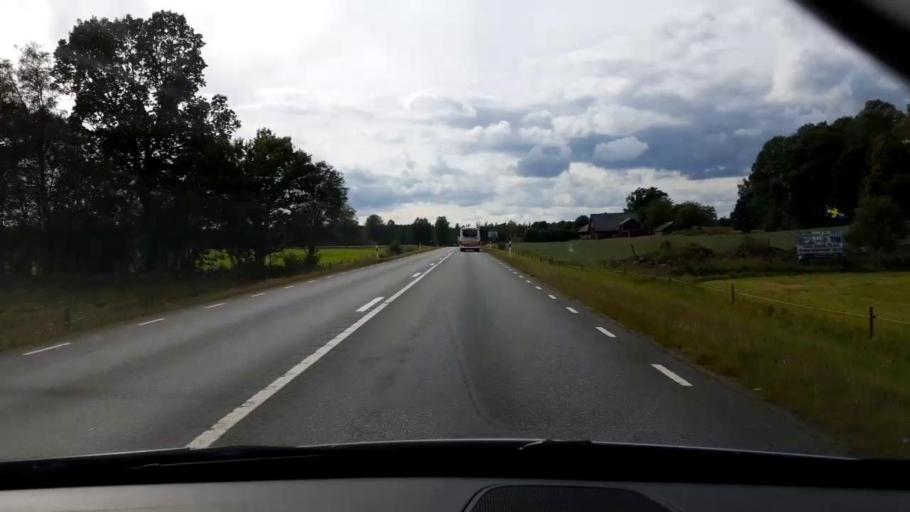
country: SE
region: Joenkoeping
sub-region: Savsjo Kommun
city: Saevsjoe
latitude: 57.3914
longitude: 14.7689
